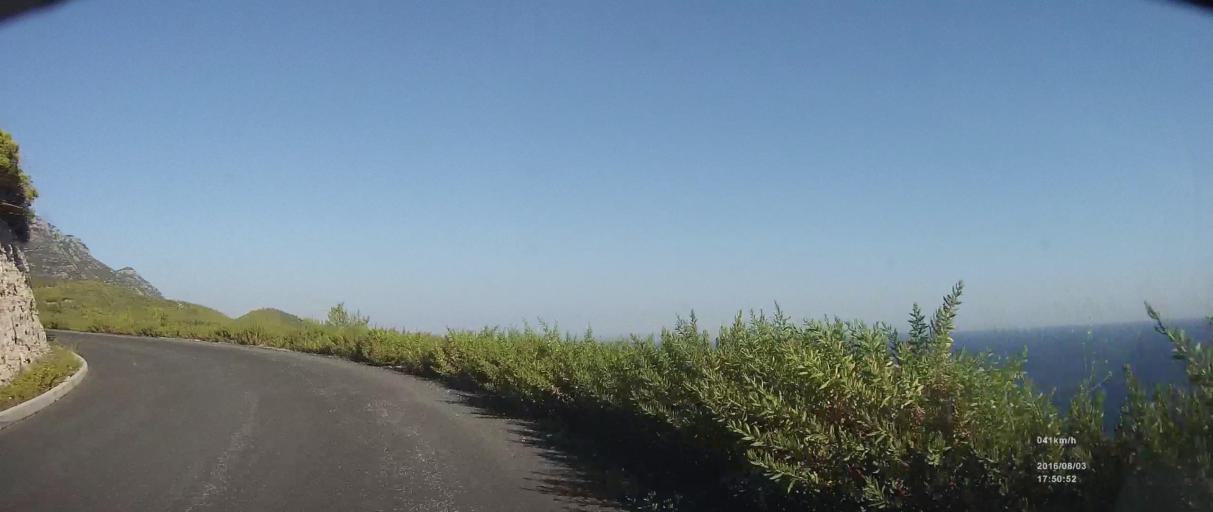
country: HR
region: Dubrovacko-Neretvanska
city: Blato
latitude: 42.7372
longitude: 17.5242
